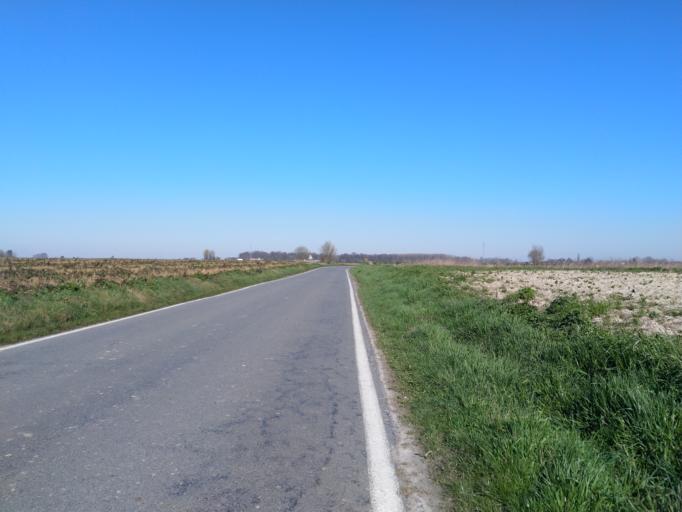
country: BE
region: Wallonia
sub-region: Province du Hainaut
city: Lens
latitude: 50.5362
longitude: 3.8593
